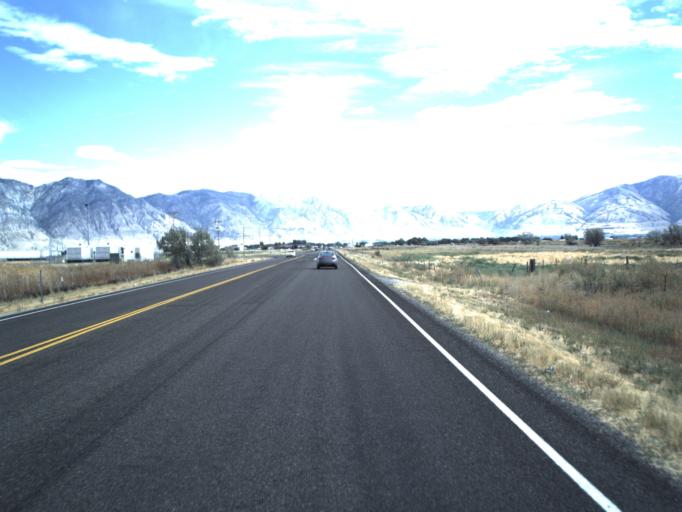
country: US
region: Utah
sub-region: Box Elder County
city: Honeyville
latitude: 41.5597
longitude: -112.1509
